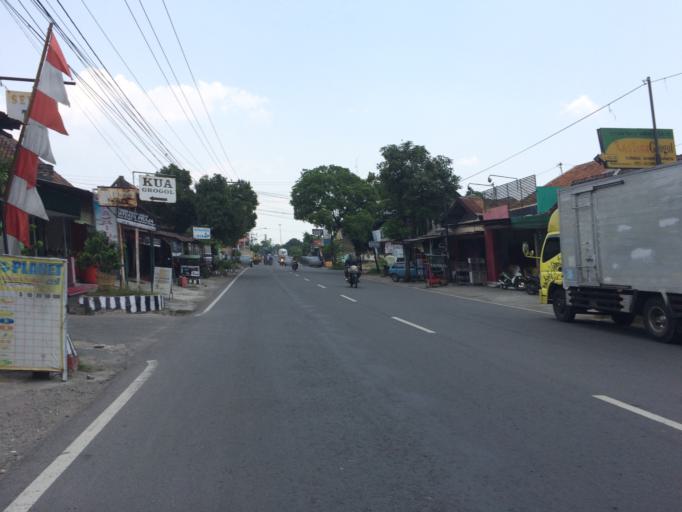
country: ID
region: Central Java
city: Grogol
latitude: -7.6081
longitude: 110.8189
